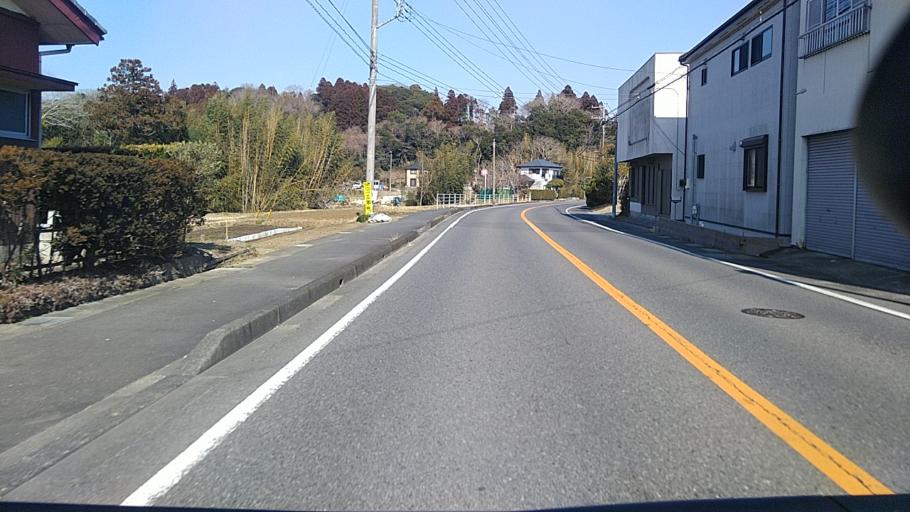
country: JP
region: Chiba
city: Mobara
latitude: 35.4085
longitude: 140.2416
